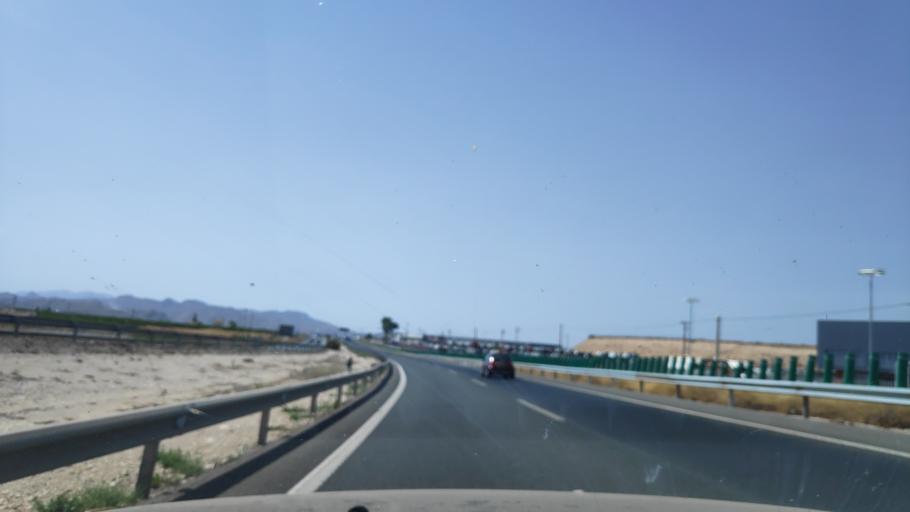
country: ES
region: Murcia
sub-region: Murcia
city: Lorqui
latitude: 38.1159
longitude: -1.2418
